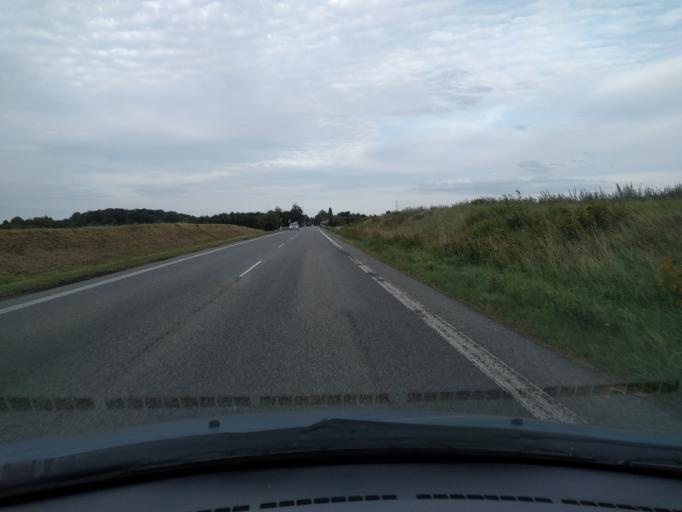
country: DK
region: Zealand
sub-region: Guldborgsund Kommune
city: Stubbekobing
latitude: 54.8909
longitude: 12.0152
